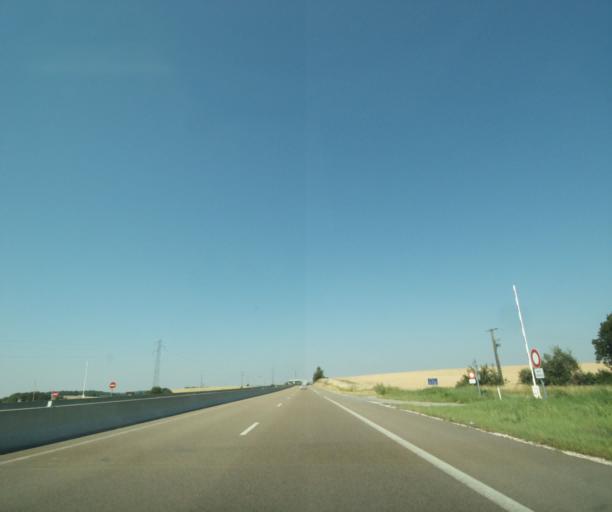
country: FR
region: Lorraine
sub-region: Departement de la Meuse
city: Ligny-en-Barrois
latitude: 48.6948
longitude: 5.3752
